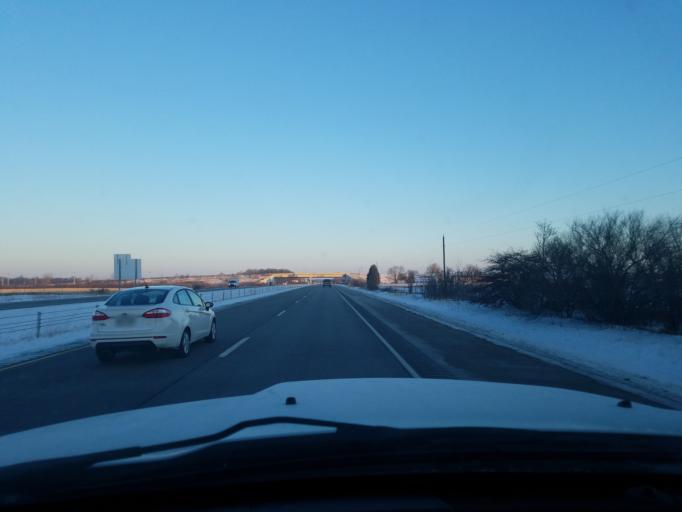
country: US
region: Indiana
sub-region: Marshall County
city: Plymouth
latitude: 41.3877
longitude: -86.2863
